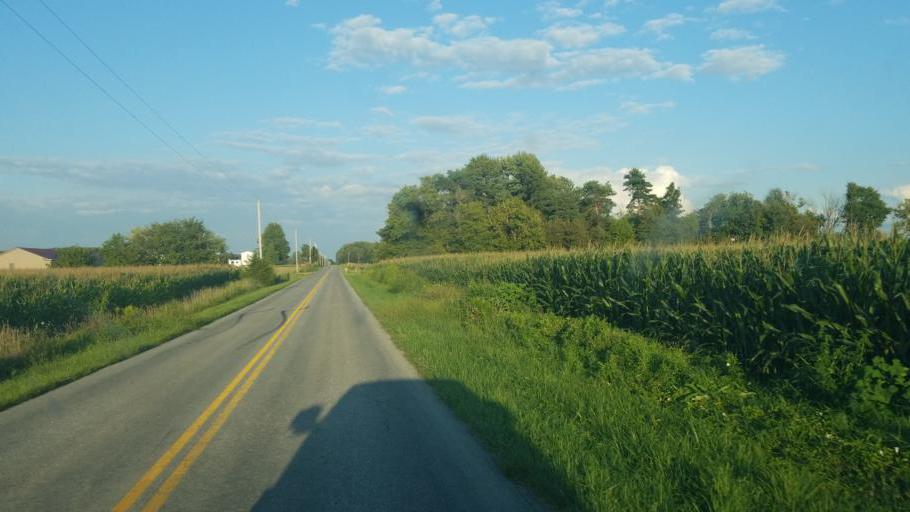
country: US
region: Ohio
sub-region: Huron County
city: Greenwich
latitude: 41.0524
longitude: -82.5670
